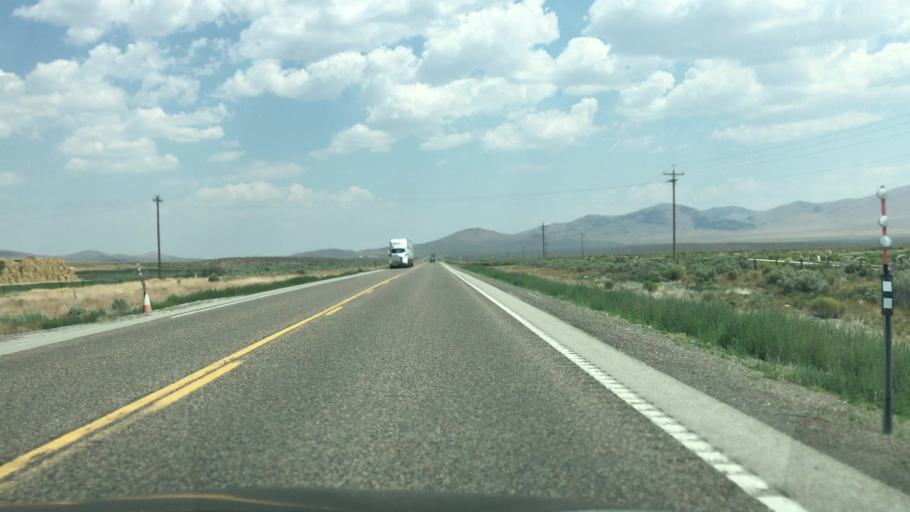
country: US
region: Nevada
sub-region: Elko County
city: Wells
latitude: 41.1438
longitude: -114.9100
